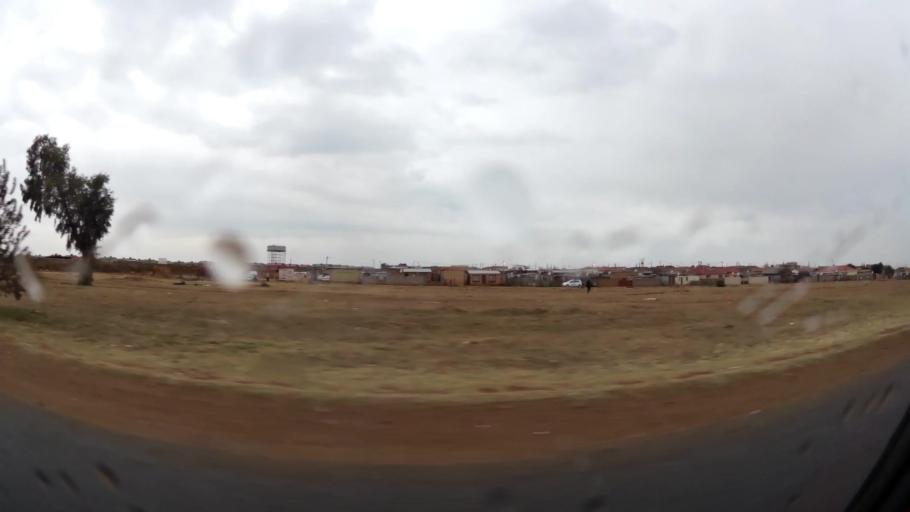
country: ZA
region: Gauteng
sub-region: City of Johannesburg Metropolitan Municipality
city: Roodepoort
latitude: -26.1721
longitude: 27.7967
